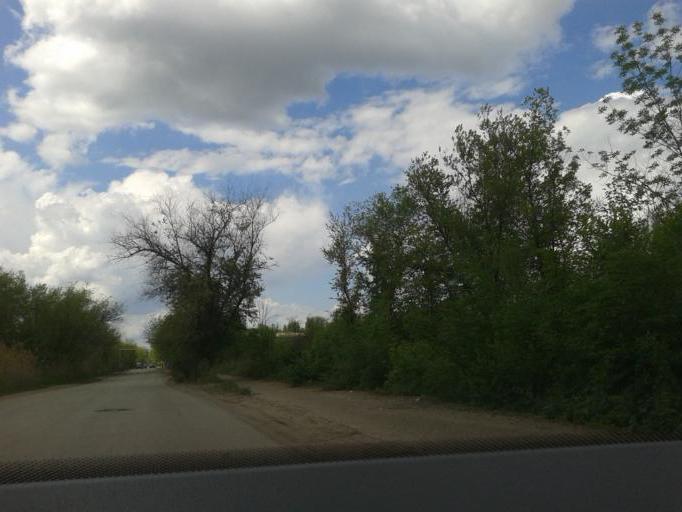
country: RU
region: Volgograd
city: Krasnoslobodsk
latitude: 48.5192
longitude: 44.5147
